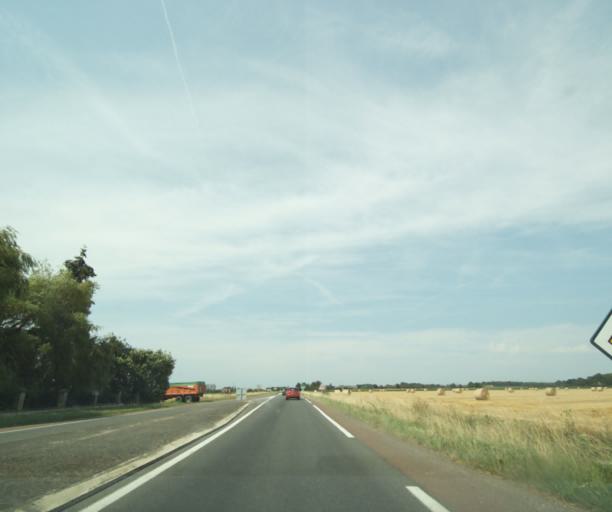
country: FR
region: Centre
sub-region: Departement d'Indre-et-Loire
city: Sorigny
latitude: 47.2000
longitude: 0.6705
